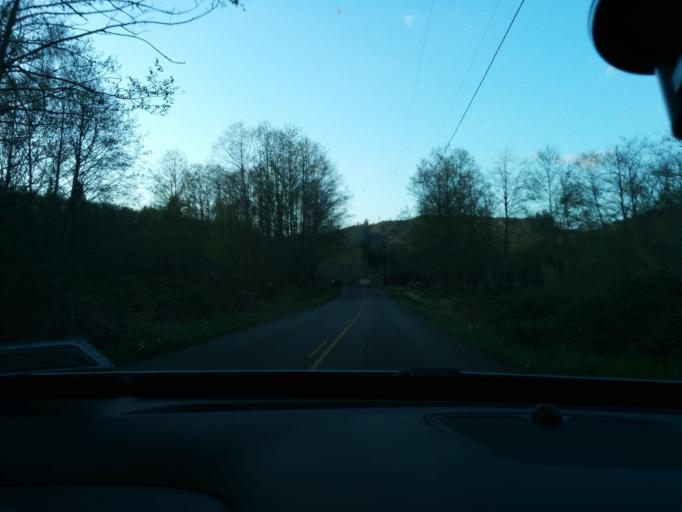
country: US
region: Washington
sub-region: Snohomish County
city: Gold Bar
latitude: 47.8816
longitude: -121.7344
